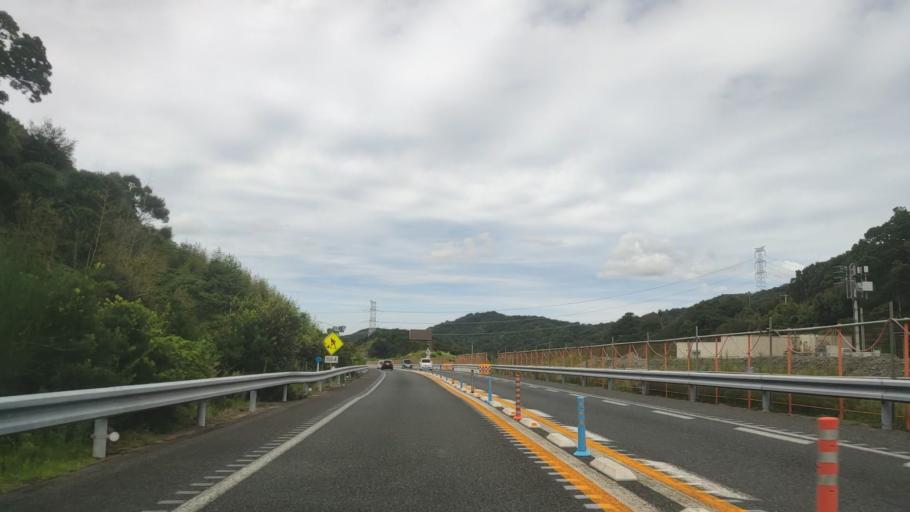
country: JP
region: Wakayama
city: Gobo
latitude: 33.8563
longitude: 135.2113
